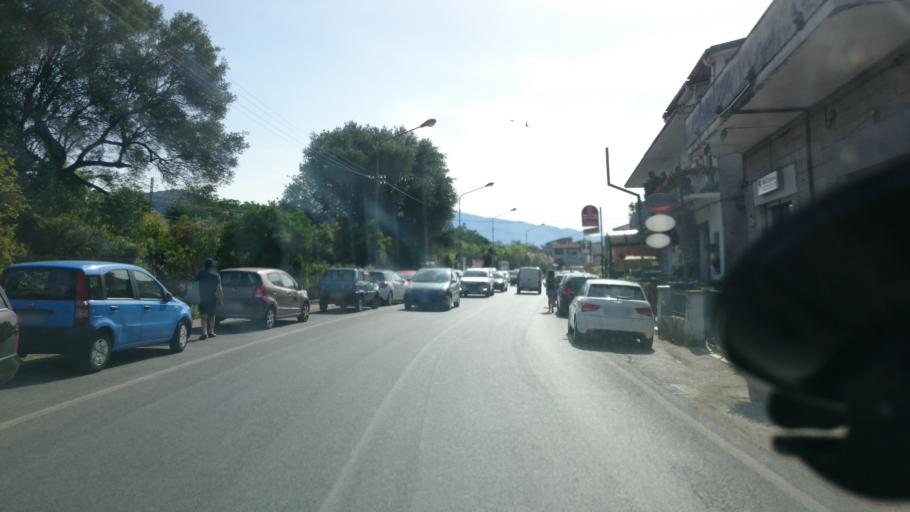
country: IT
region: Campania
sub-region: Provincia di Salerno
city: Policastro Bussentino
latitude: 40.0740
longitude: 15.5188
